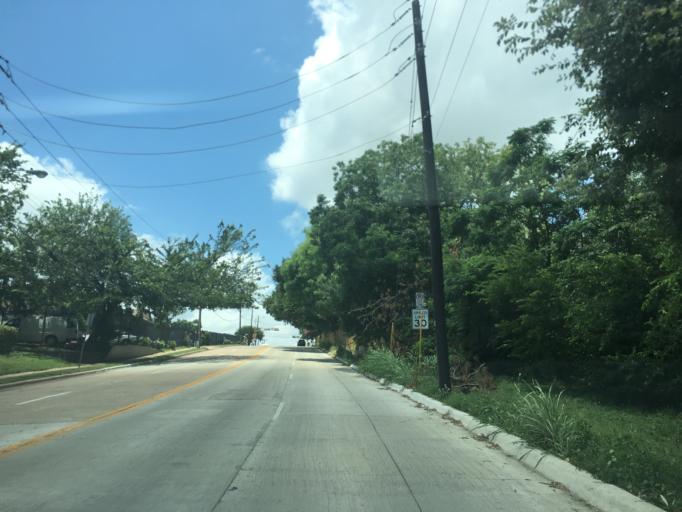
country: US
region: Texas
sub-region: Dallas County
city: University Park
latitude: 32.8745
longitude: -96.7534
